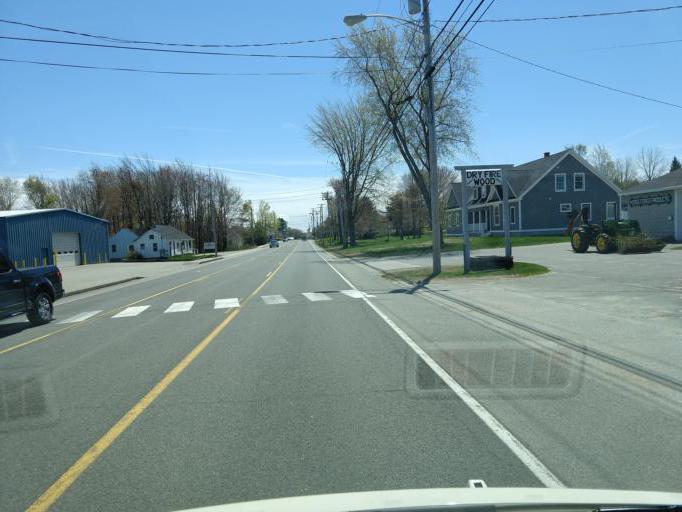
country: US
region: Maine
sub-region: York County
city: Wells Beach Station
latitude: 43.3124
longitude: -70.5848
